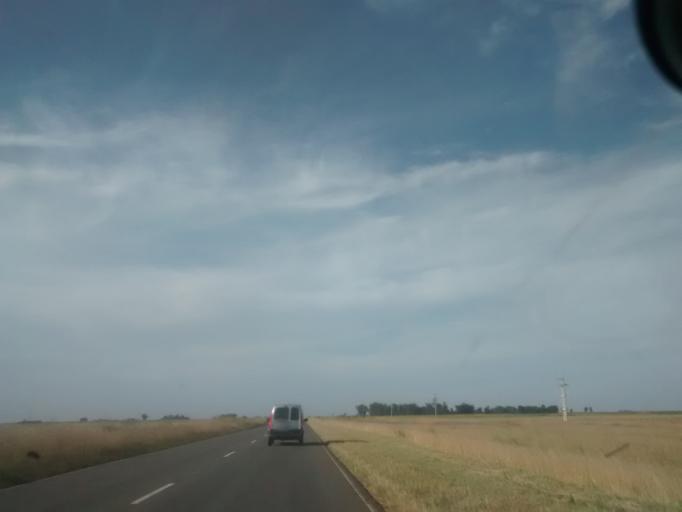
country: AR
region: Buenos Aires
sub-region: Partido de Ayacucho
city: Ayacucho
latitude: -37.0731
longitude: -58.5447
